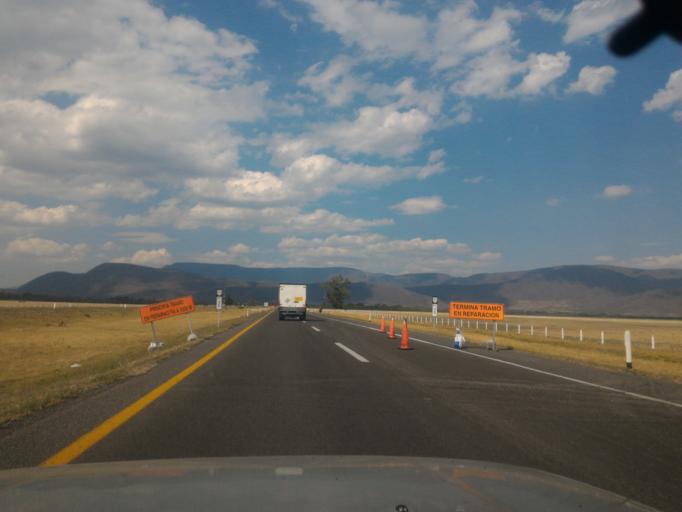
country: MX
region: Jalisco
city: Zacoalco de Torres
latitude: 20.1394
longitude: -103.5052
